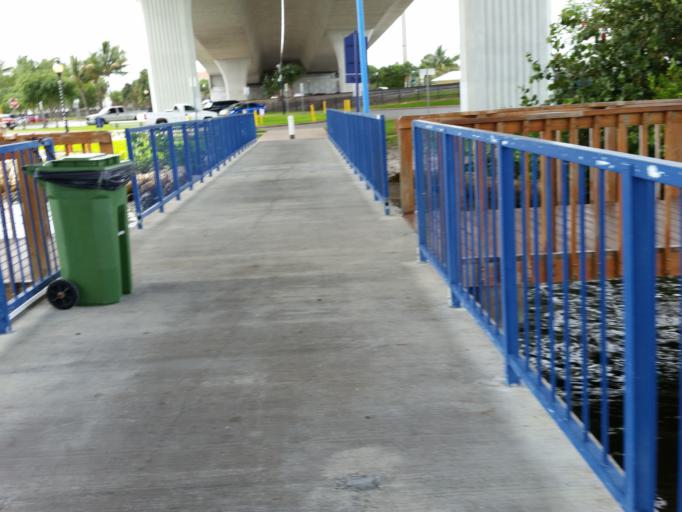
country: US
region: Florida
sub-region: Martin County
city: Stuart
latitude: 27.2026
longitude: -80.2581
